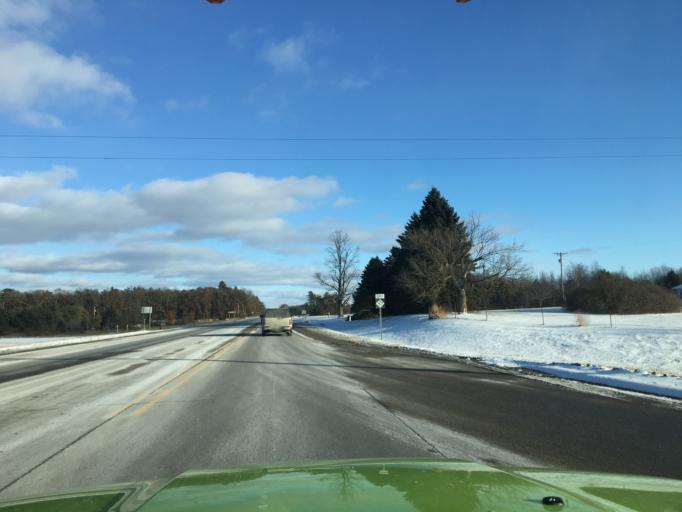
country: US
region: Michigan
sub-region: Kent County
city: Cedar Springs
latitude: 43.1758
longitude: -85.4908
